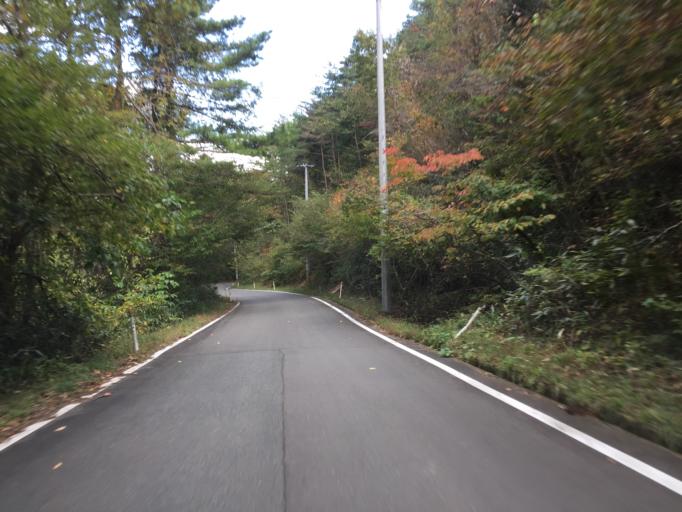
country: JP
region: Miyagi
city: Marumori
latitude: 37.8239
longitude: 140.8066
